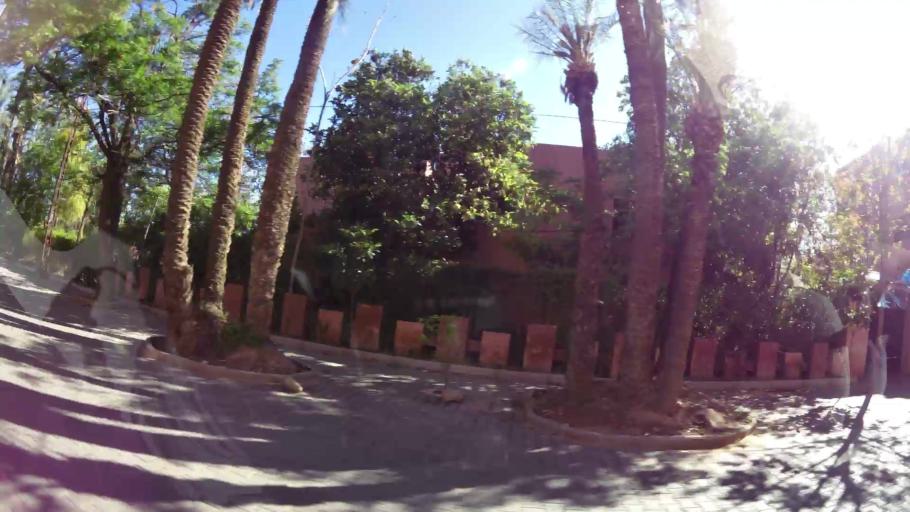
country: MA
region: Marrakech-Tensift-Al Haouz
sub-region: Marrakech
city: Marrakesh
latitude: 31.6398
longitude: -8.0123
